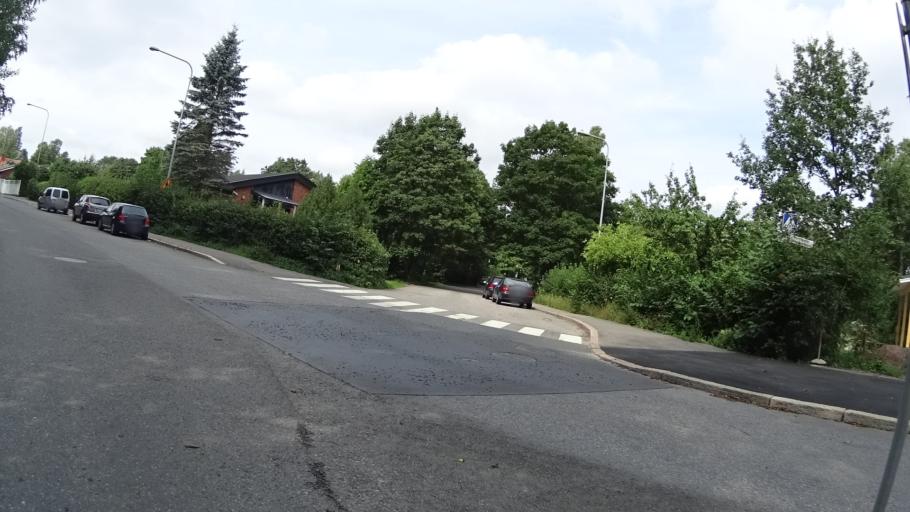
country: FI
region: Uusimaa
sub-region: Helsinki
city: Teekkarikylae
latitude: 60.2259
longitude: 24.8469
